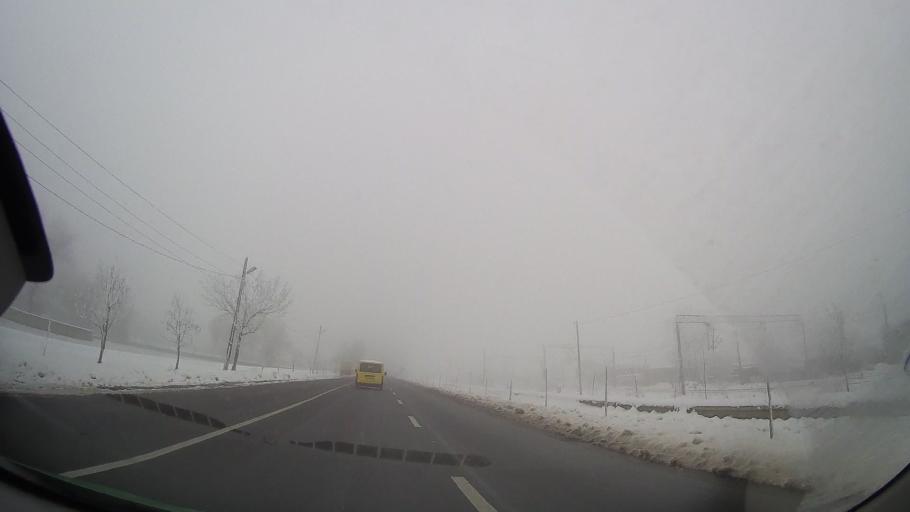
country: RO
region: Iasi
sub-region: Municipiul Pascani
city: Pascani
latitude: 47.2454
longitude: 26.7307
